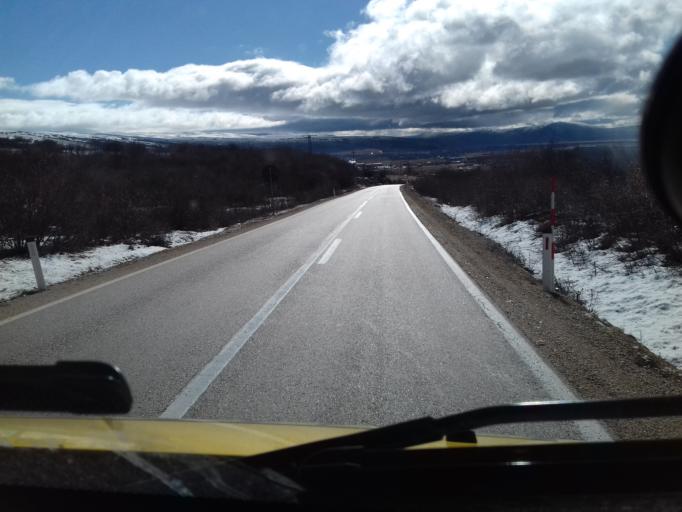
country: BA
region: Federation of Bosnia and Herzegovina
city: Tomislavgrad
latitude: 43.7801
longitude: 17.2246
